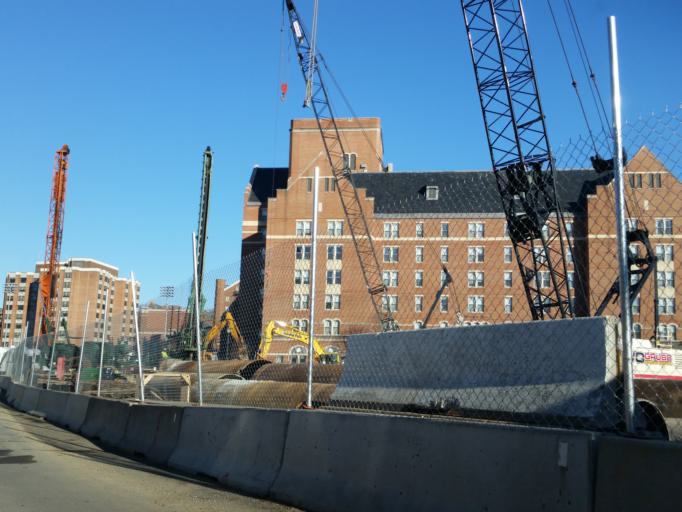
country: US
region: Virginia
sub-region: Arlington County
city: Arlington
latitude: 38.9071
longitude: -77.0771
